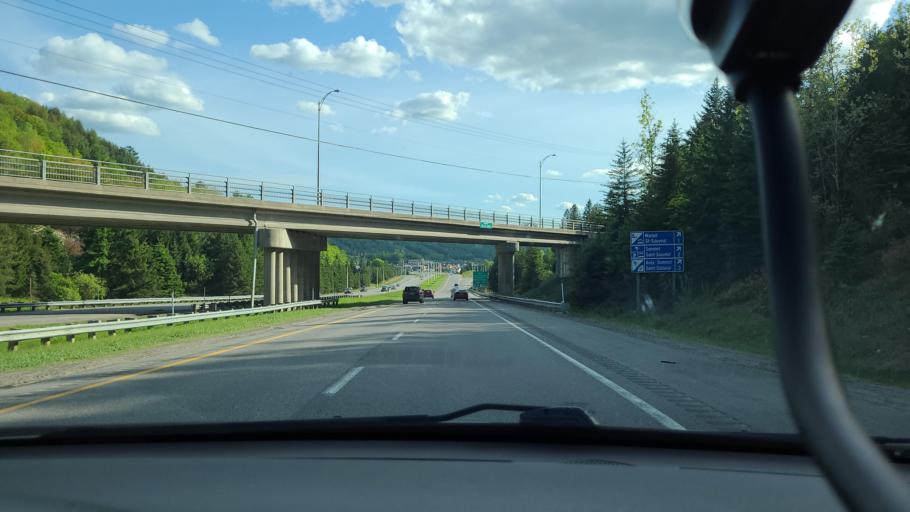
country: CA
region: Quebec
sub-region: Laurentides
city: Saint-Sauveur
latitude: 45.9012
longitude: -74.1430
